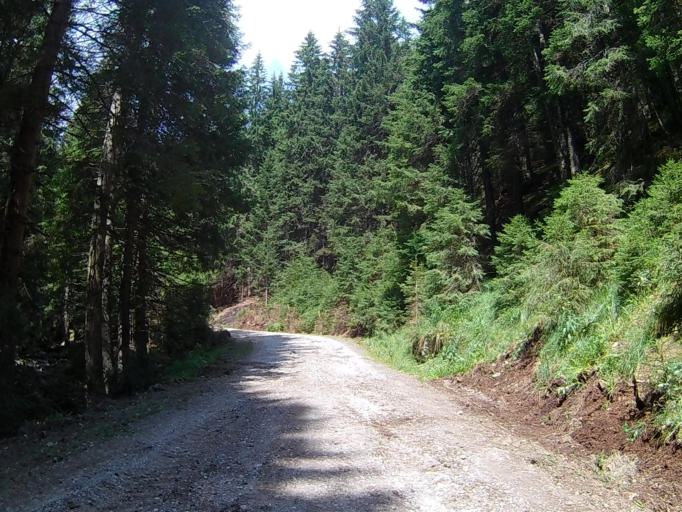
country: SI
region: Lovrenc na Pohorju
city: Lovrenc na Pohorju
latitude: 46.4776
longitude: 15.4206
